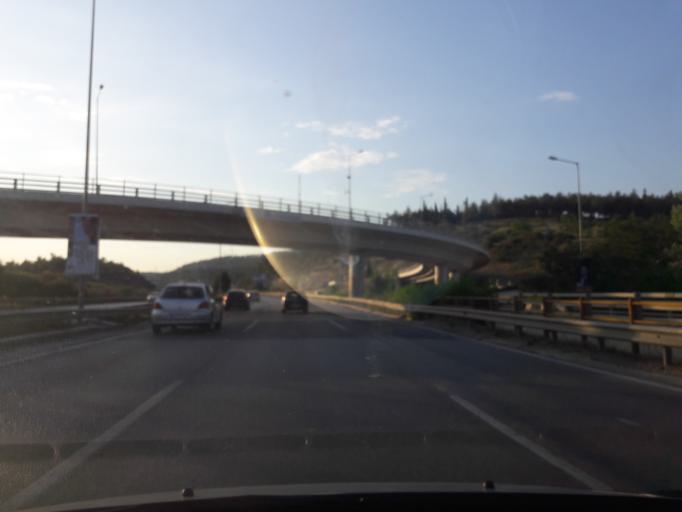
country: GR
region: Central Macedonia
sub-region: Nomos Thessalonikis
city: Triandria
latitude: 40.6218
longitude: 22.9823
